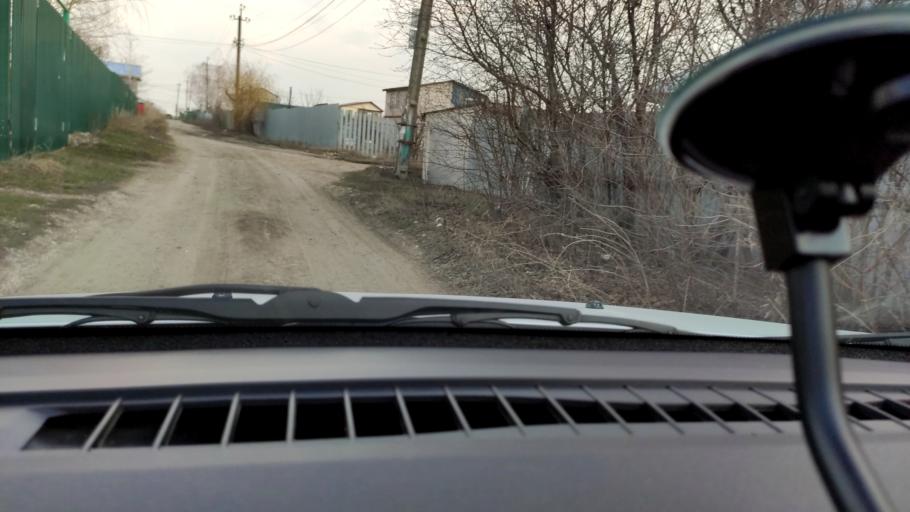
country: RU
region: Samara
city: Smyshlyayevka
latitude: 53.0919
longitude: 50.3935
